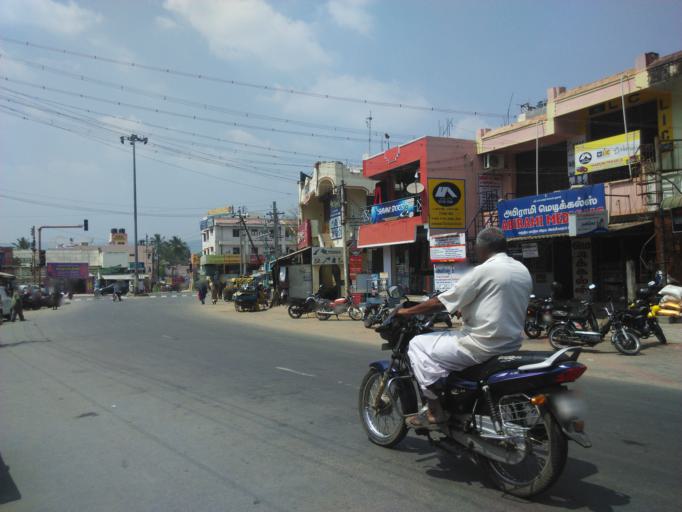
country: IN
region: Tamil Nadu
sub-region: Coimbatore
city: Periyanayakkanpalaiyam
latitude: 11.1527
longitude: 76.9450
